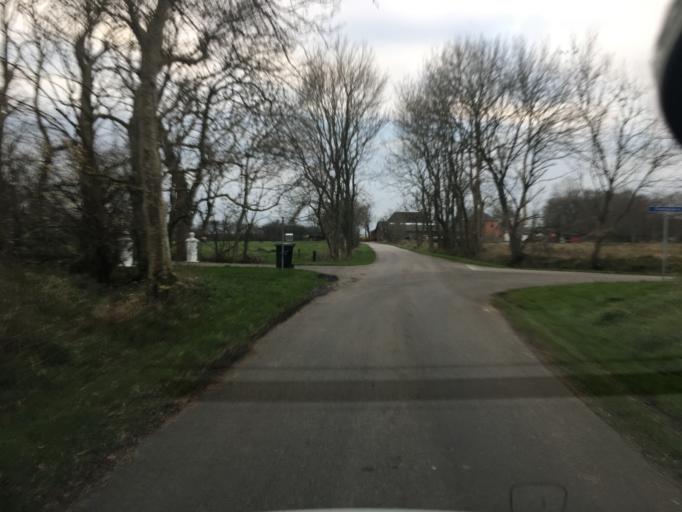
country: DK
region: South Denmark
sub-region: Tonder Kommune
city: Toftlund
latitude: 55.0714
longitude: 9.0754
